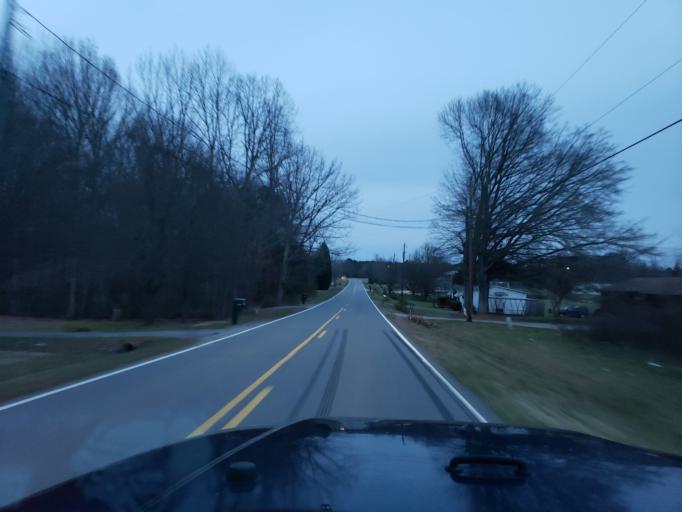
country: US
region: North Carolina
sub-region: Cleveland County
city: White Plains
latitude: 35.1939
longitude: -81.4415
